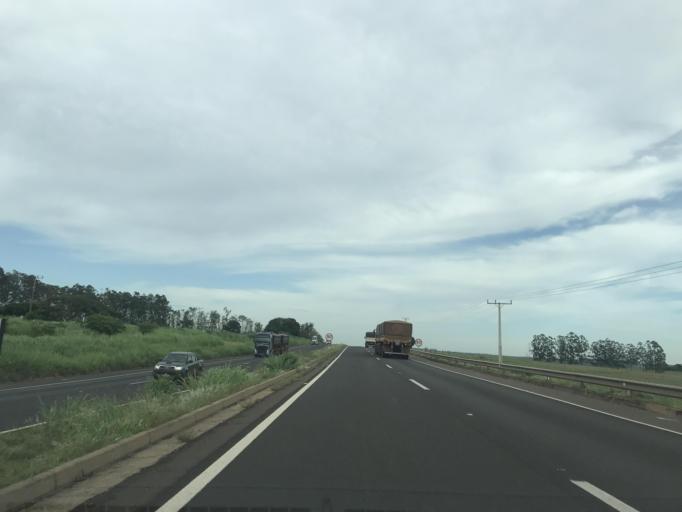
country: BR
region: Parana
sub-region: Alto Parana
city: Alto Parana
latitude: -23.1194
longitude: -52.3173
